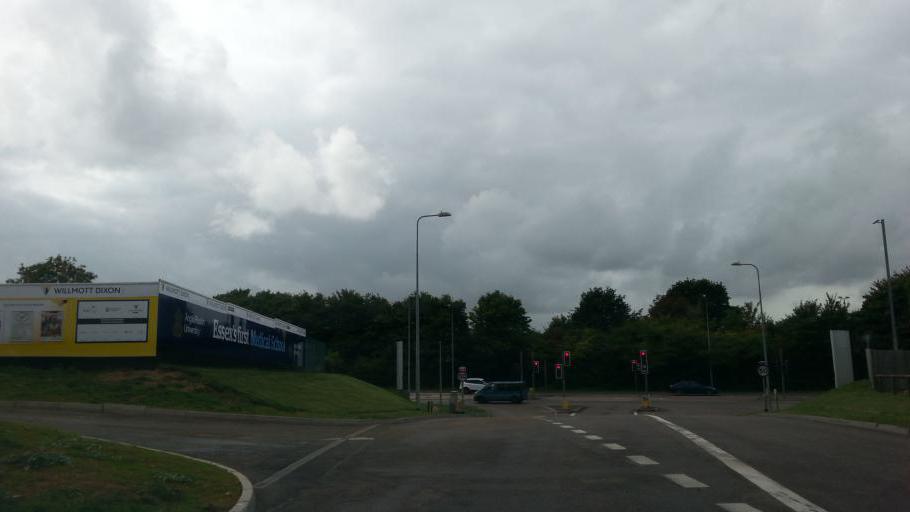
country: GB
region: England
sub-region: Essex
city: Chelmsford
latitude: 51.7437
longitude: 0.4711
